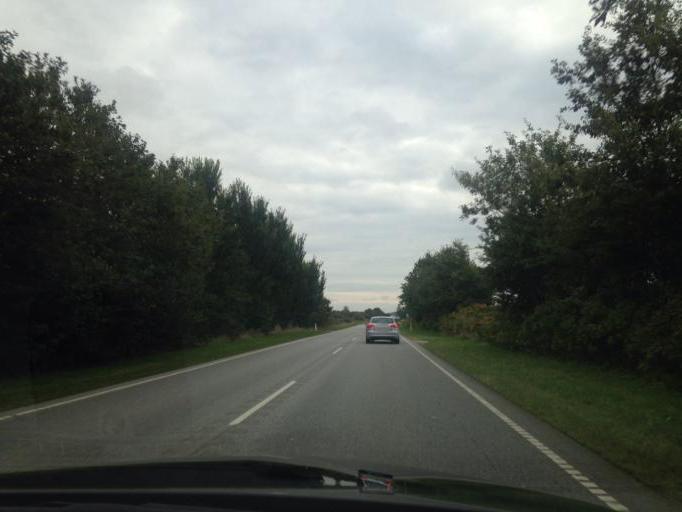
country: DK
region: South Denmark
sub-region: Haderslev Kommune
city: Vojens
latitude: 55.2489
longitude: 9.3787
